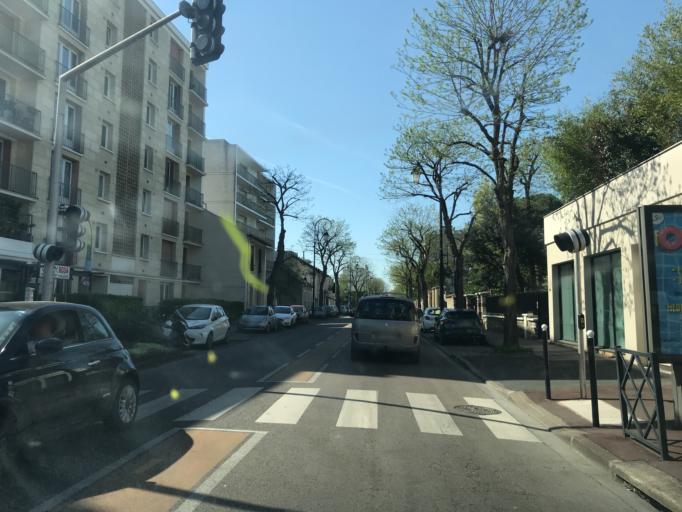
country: FR
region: Ile-de-France
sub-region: Departement du Val-de-Marne
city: Saint-Maur-des-Fosses
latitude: 48.8000
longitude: 2.4975
